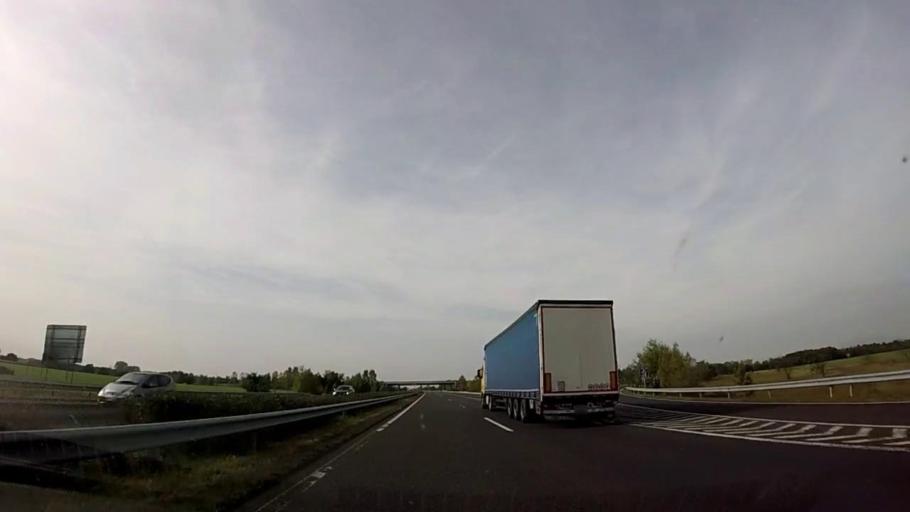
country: HU
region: Somogy
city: Balatonboglar
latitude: 46.7552
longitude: 17.6326
